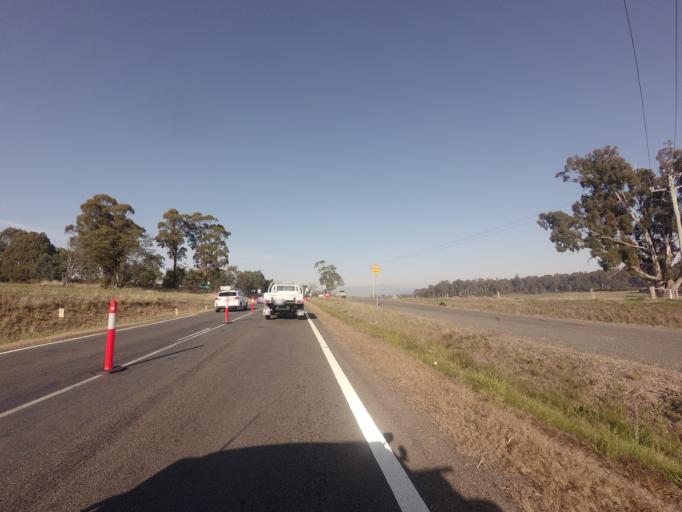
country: AU
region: Tasmania
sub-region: Northern Midlands
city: Longford
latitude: -41.5543
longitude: 146.9883
